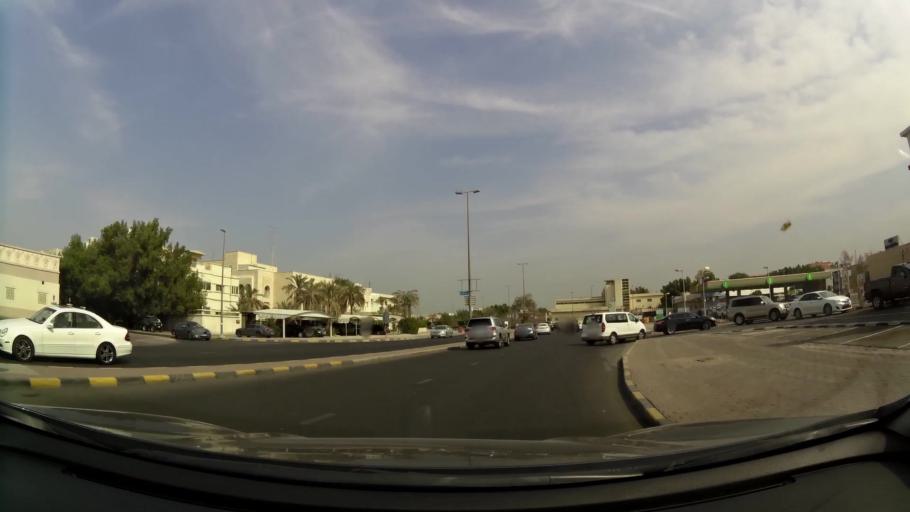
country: KW
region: Al Asimah
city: Ash Shamiyah
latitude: 29.3386
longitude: 47.9642
